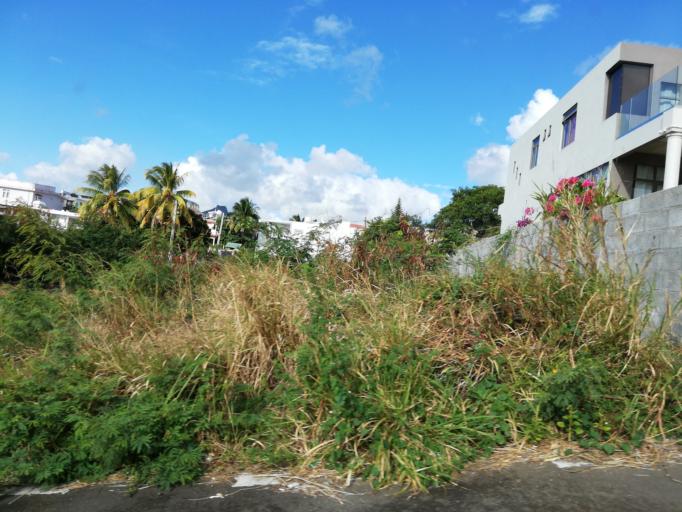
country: MU
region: Black River
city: Petite Riviere
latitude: -20.2023
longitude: 57.4639
